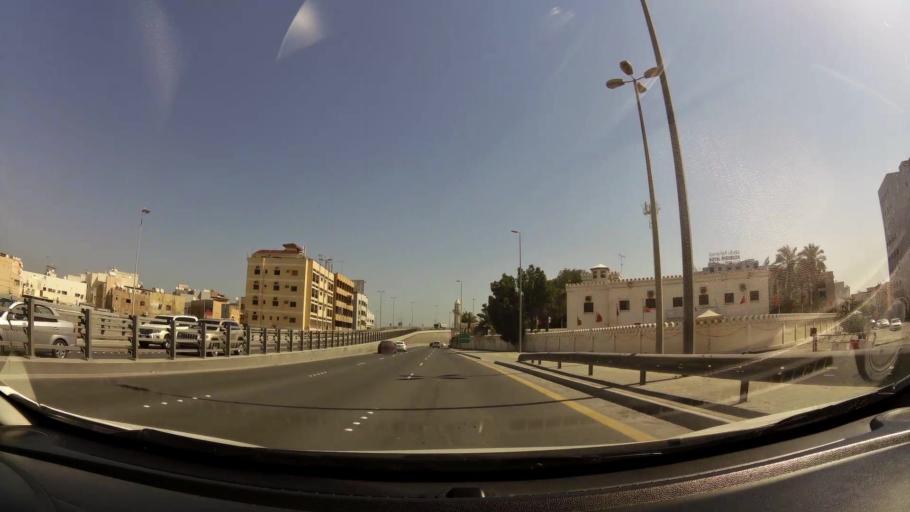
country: BH
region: Manama
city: Manama
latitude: 26.2054
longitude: 50.5998
